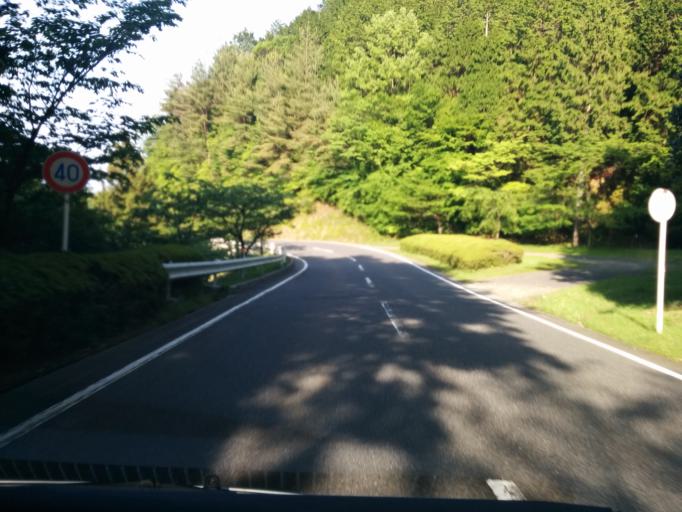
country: JP
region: Shiga Prefecture
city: Kitahama
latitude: 35.1045
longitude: 135.8555
